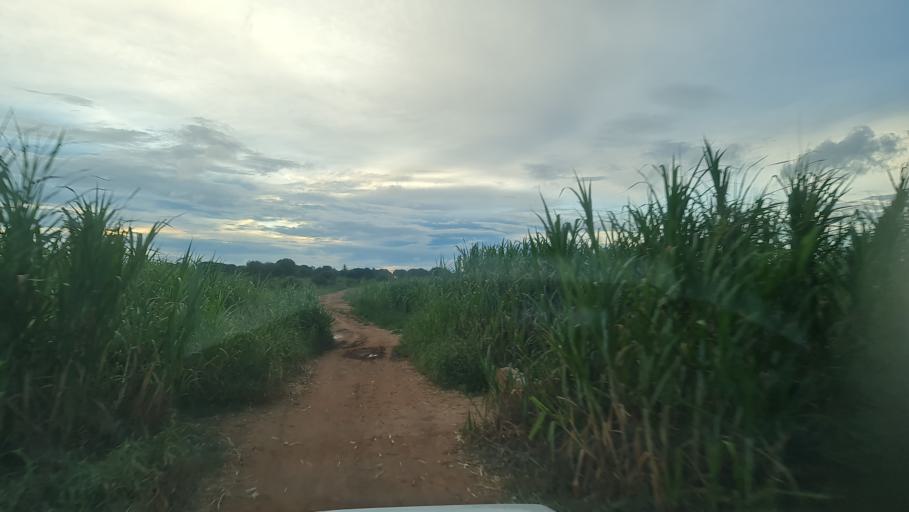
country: MZ
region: Nampula
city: Nacala
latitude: -14.7419
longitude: 39.9481
